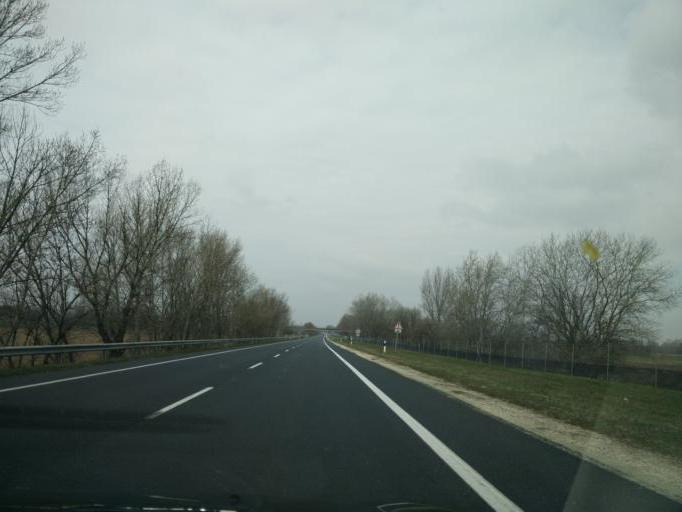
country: HU
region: Gyor-Moson-Sopron
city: Toltestava
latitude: 47.6979
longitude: 17.7760
